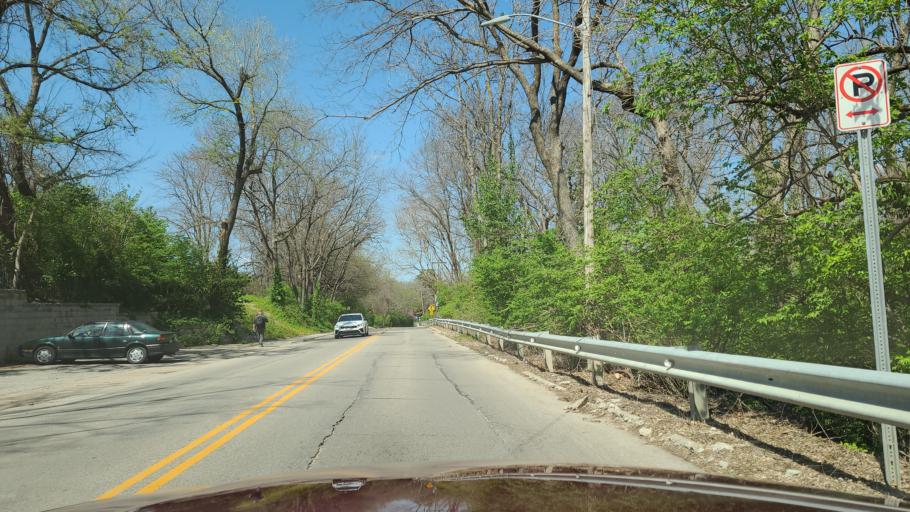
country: US
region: Kansas
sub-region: Douglas County
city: Lawrence
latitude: 38.9635
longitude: -95.2535
